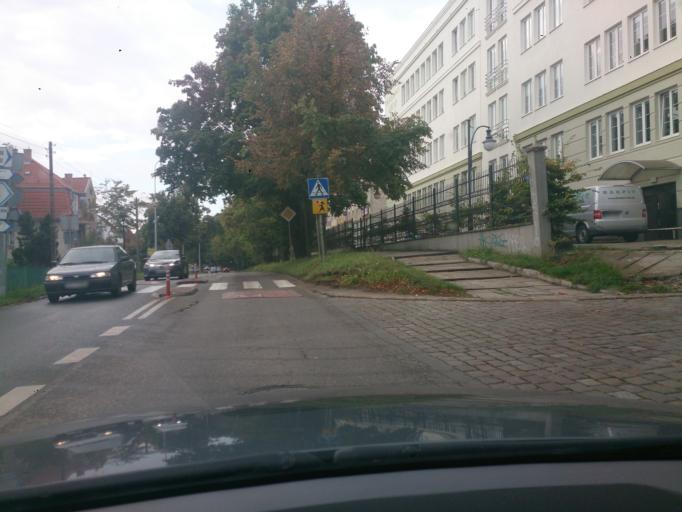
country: PL
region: Pomeranian Voivodeship
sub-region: Sopot
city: Sopot
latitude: 54.4033
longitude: 18.5608
